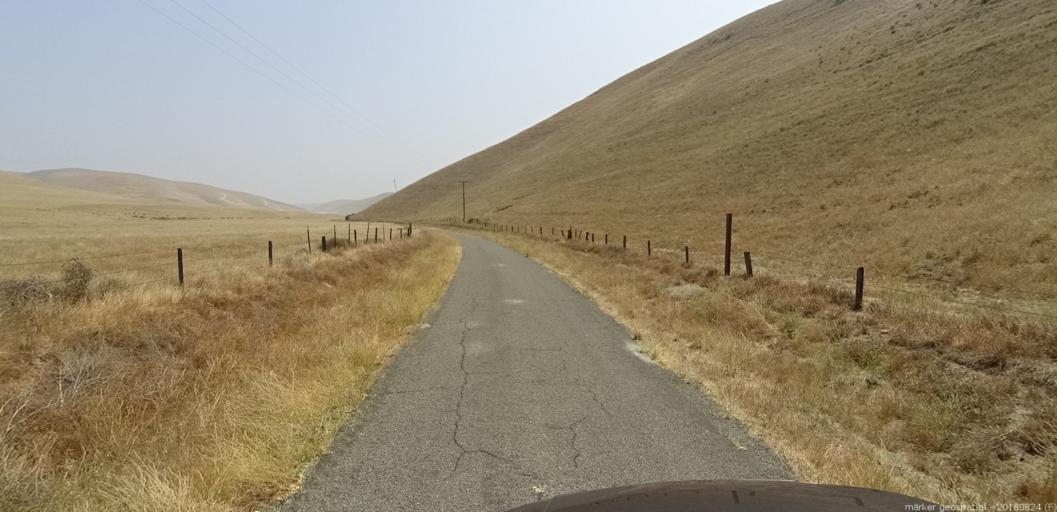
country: US
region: California
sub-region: Monterey County
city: King City
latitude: 36.1937
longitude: -120.9983
